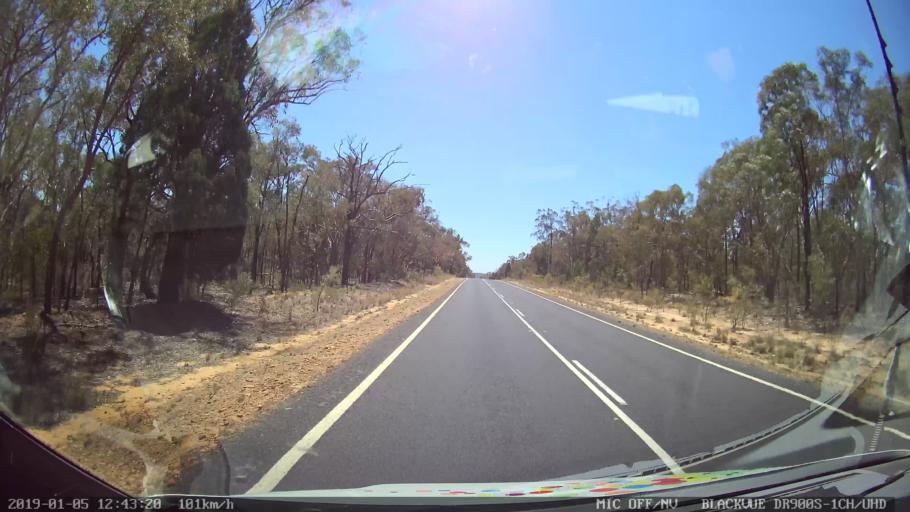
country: AU
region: New South Wales
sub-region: Warrumbungle Shire
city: Coonabarabran
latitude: -31.1491
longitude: 149.5228
